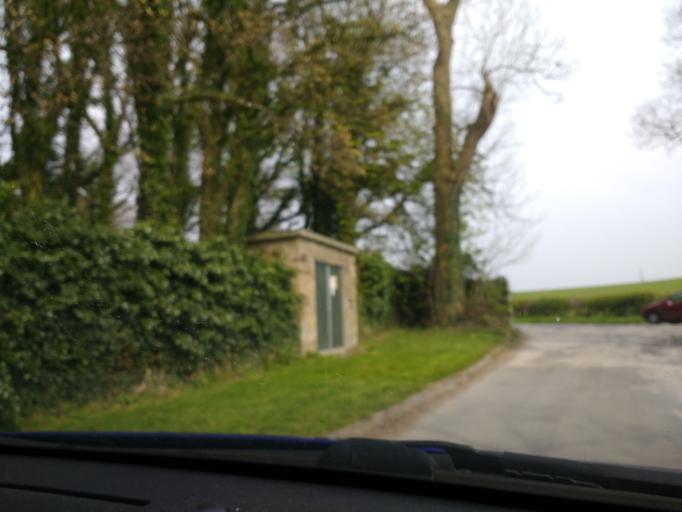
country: GB
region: England
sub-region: Lancashire
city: Galgate
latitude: 54.0068
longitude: -2.8206
